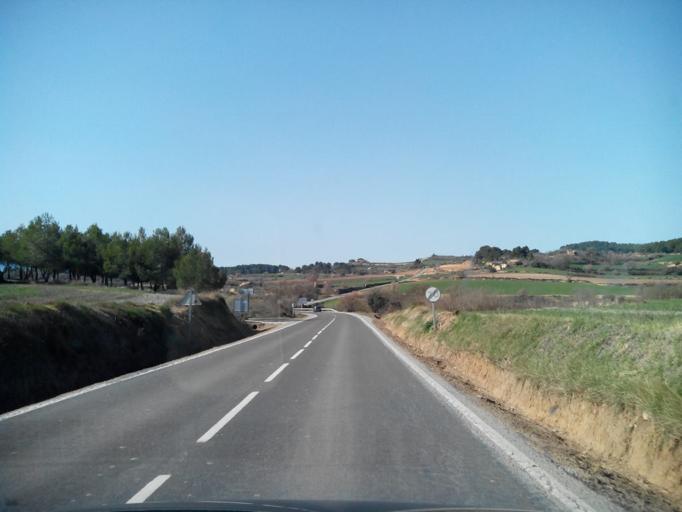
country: ES
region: Catalonia
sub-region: Provincia de Tarragona
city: Conesa
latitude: 41.4755
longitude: 1.2803
